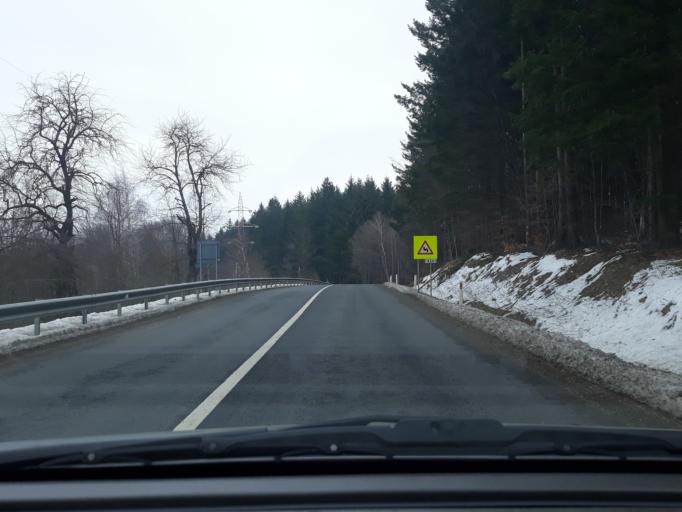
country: RO
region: Bihor
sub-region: Comuna Sinteu
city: Sinteu
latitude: 47.1206
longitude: 22.4420
